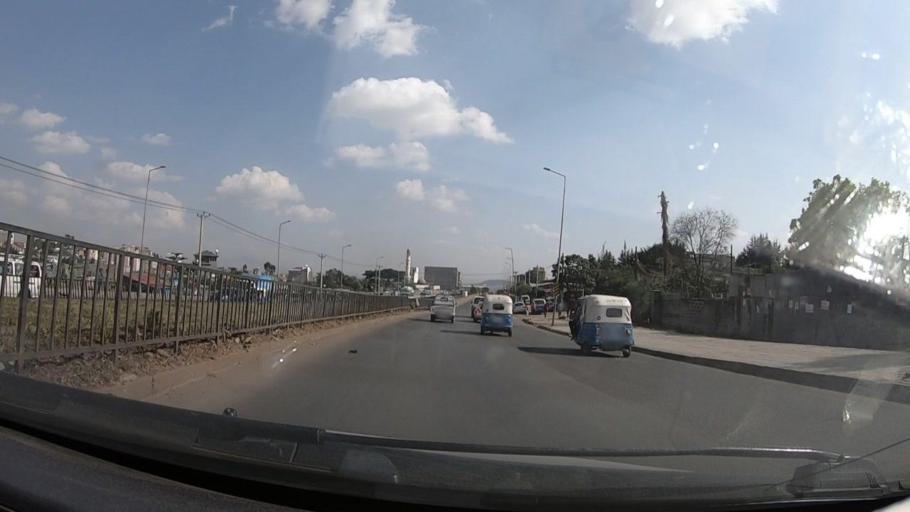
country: ET
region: Adis Abeba
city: Addis Ababa
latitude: 8.9906
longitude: 38.6904
